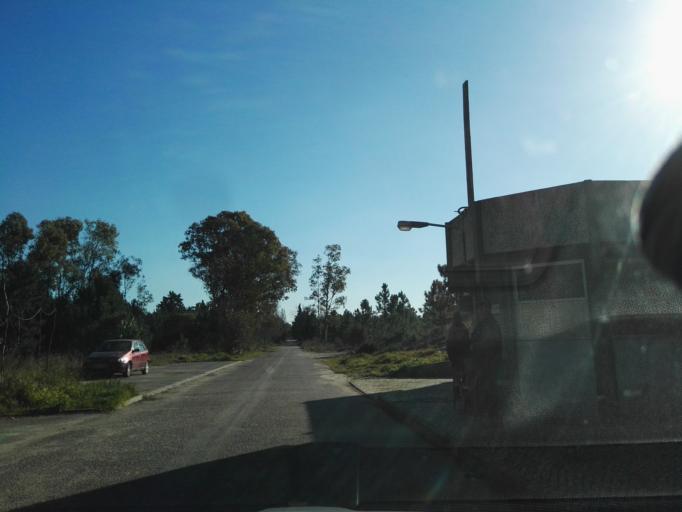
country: PT
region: Setubal
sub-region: Seixal
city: Corroios
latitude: 38.6253
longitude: -9.1458
